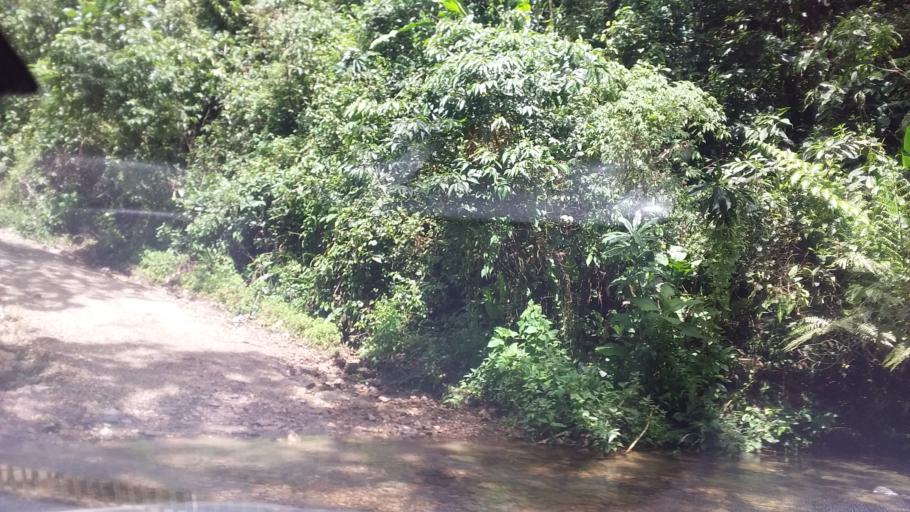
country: CO
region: Casanare
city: Nunchia
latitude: 5.6281
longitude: -72.3307
